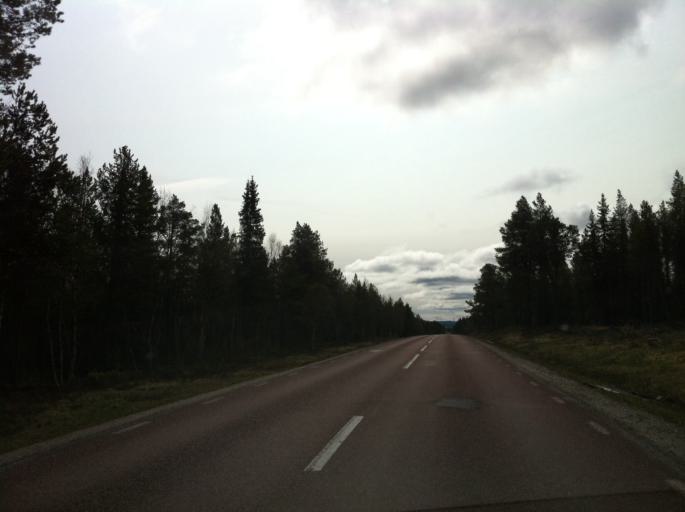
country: NO
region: Hedmark
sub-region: Engerdal
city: Engerdal
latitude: 62.4828
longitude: 12.6595
